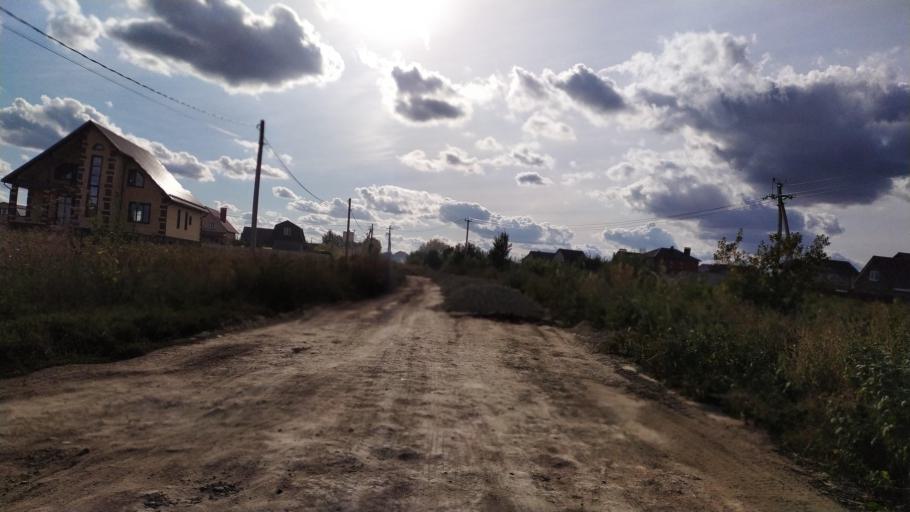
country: RU
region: Kursk
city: Kursk
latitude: 51.6403
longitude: 36.1547
